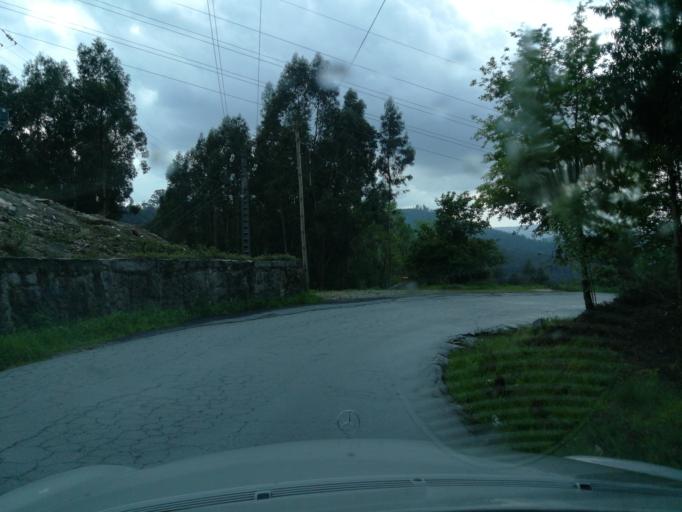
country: PT
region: Braga
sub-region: Vila Nova de Famalicao
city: Joane
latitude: 41.4677
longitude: -8.4294
